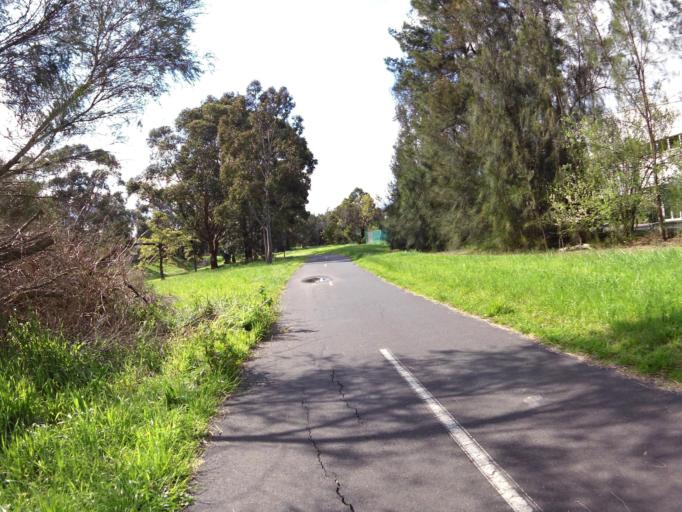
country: AU
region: Victoria
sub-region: Maroondah
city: Bayswater North
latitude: -37.8346
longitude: 145.2804
